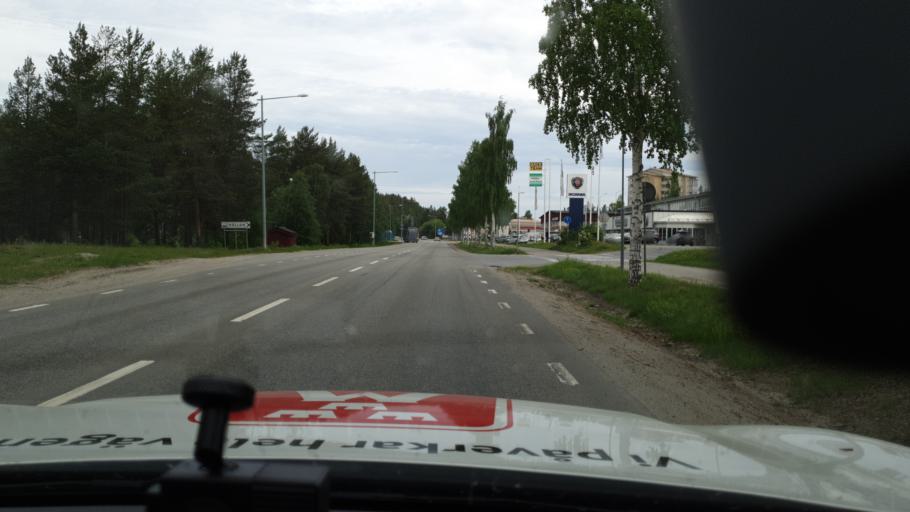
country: SE
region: Vaesterbotten
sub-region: Lycksele Kommun
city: Lycksele
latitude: 64.5877
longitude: 18.6931
